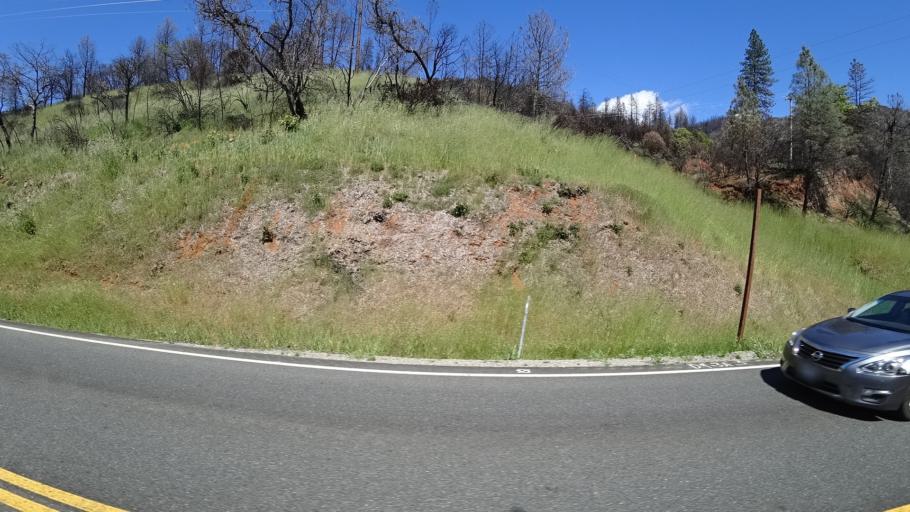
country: US
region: California
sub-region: Trinity County
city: Weaverville
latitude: 40.7664
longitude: -123.0832
